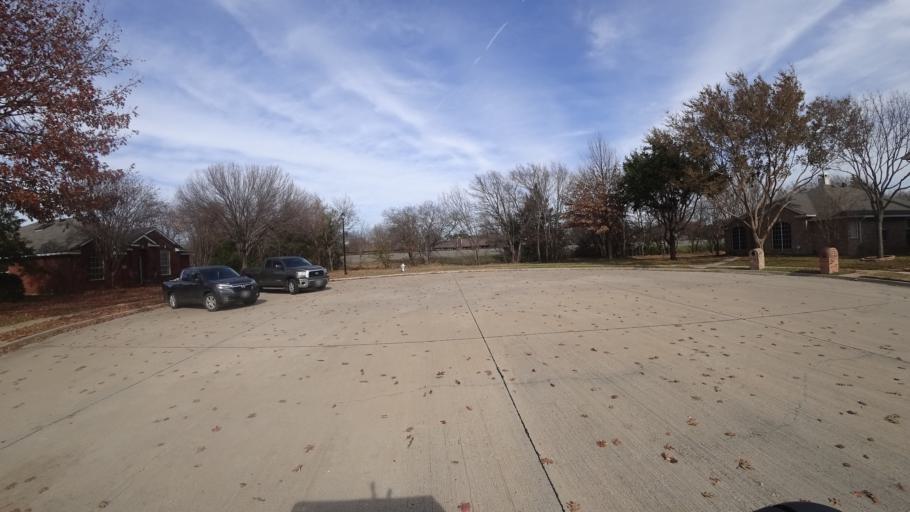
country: US
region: Texas
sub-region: Denton County
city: Highland Village
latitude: 33.0683
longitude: -97.0409
